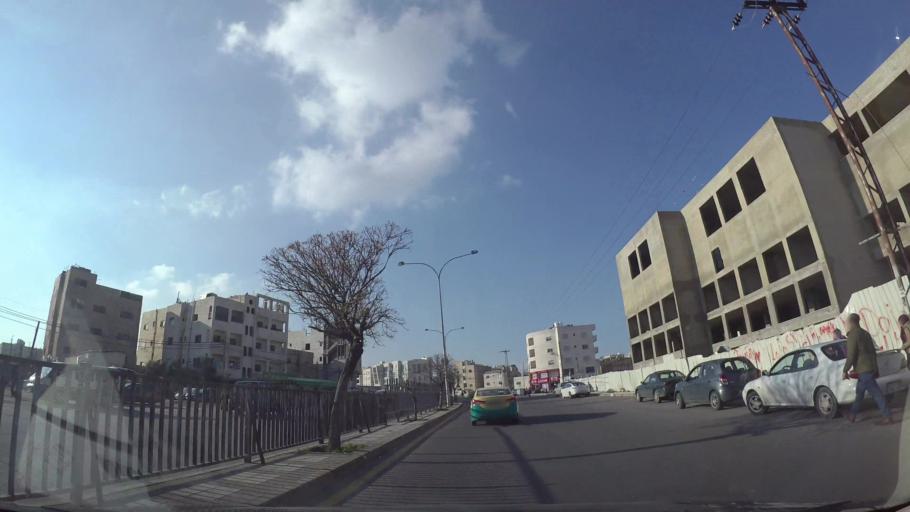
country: JO
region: Amman
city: Amman
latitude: 31.9779
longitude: 35.9438
